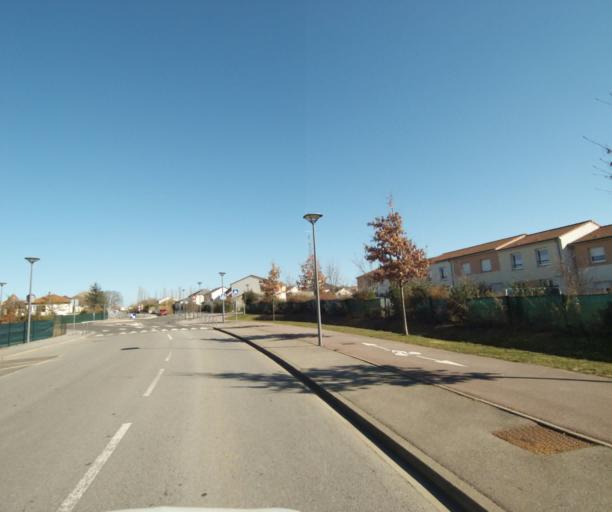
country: FR
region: Lorraine
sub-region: Departement de Meurthe-et-Moselle
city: Tomblaine
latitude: 48.6756
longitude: 6.2289
